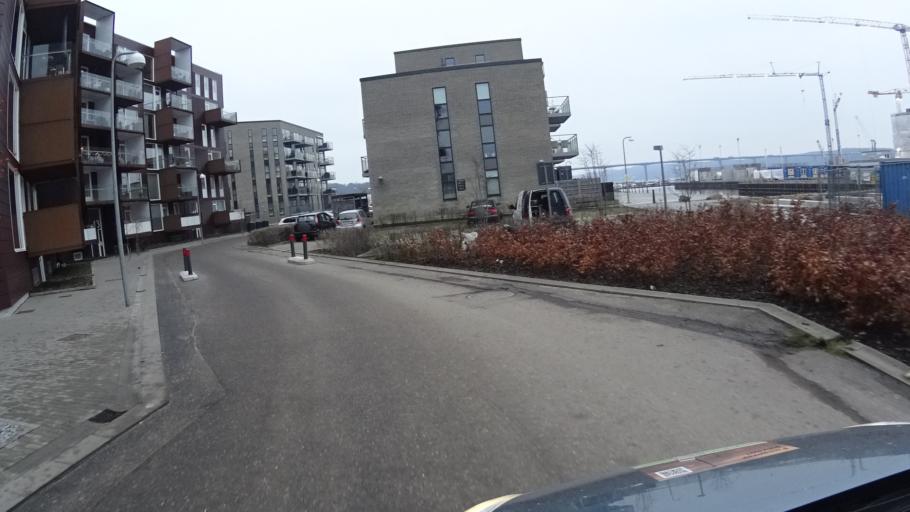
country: DK
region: South Denmark
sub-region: Vejle Kommune
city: Vejle
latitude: 55.7081
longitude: 9.5530
